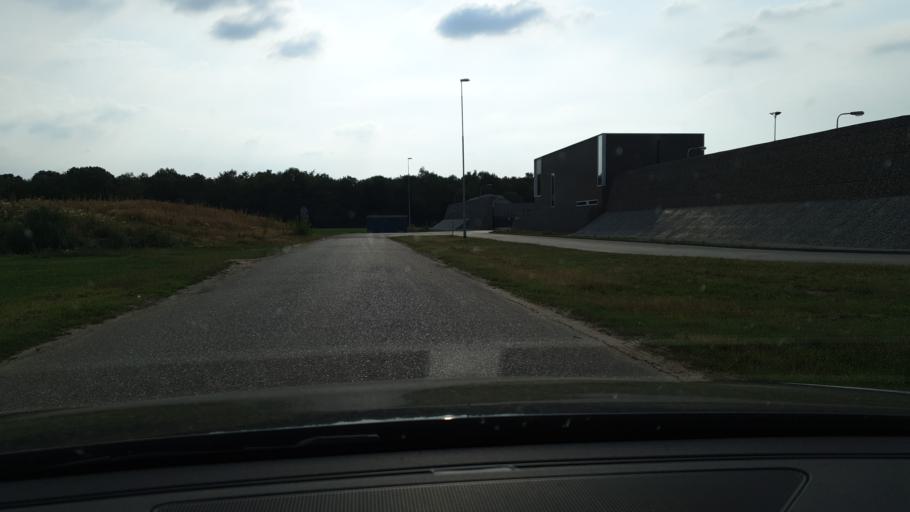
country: NL
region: North Brabant
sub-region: Gemeente Veldhoven
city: Oerle
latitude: 51.4396
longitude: 5.3822
